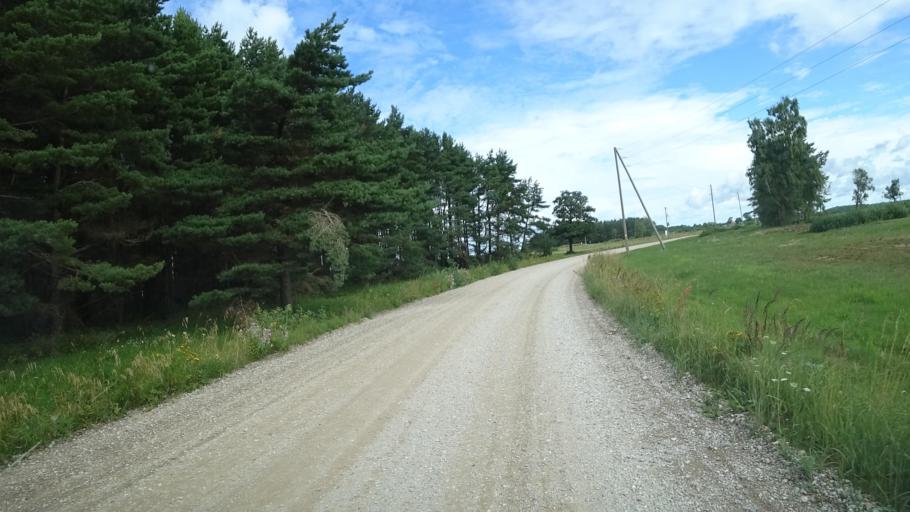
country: LV
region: Liepaja
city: Vec-Liepaja
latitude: 56.6411
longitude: 21.0445
